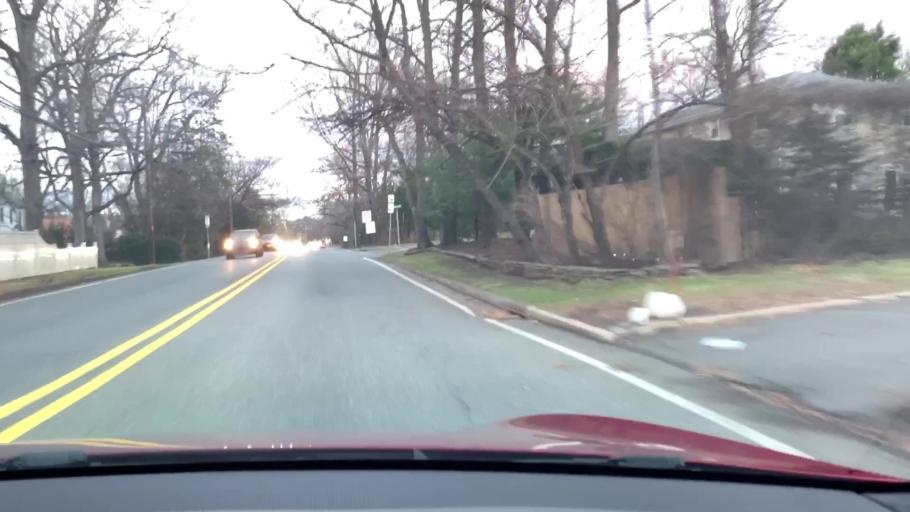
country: US
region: New Jersey
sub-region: Bergen County
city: Tenafly
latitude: 40.9342
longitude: -73.9774
